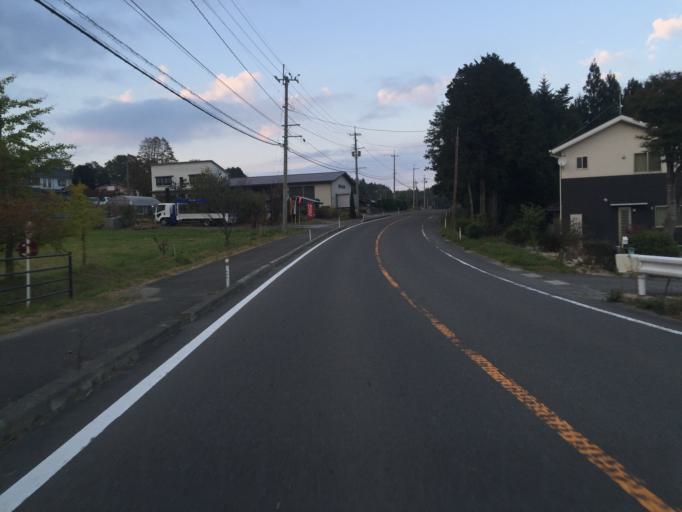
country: JP
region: Fukushima
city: Nihommatsu
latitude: 37.6155
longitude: 140.3587
